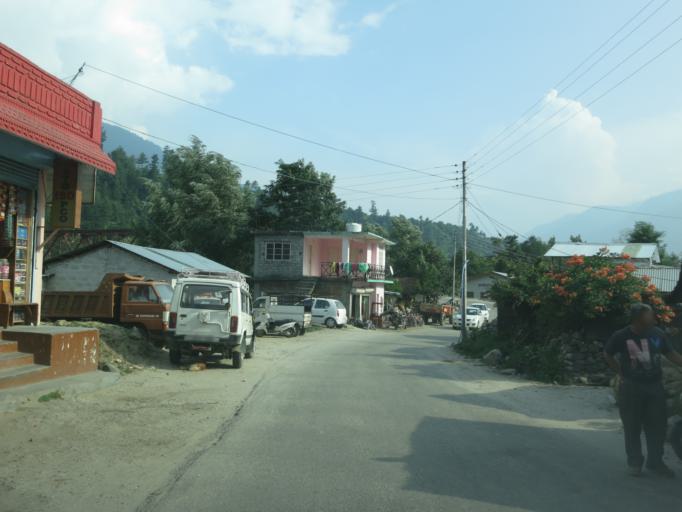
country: IN
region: Himachal Pradesh
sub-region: Kulu
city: Nagar
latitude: 32.1094
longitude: 77.1494
